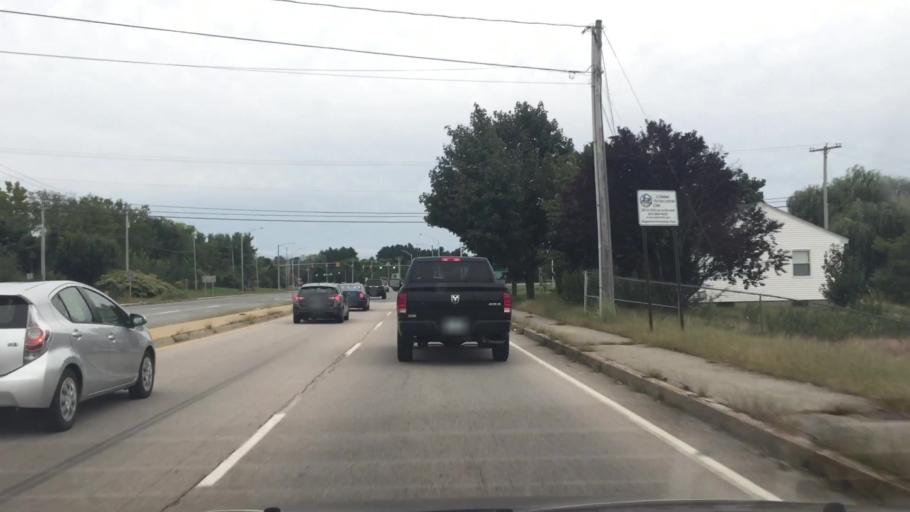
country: US
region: New Hampshire
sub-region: Hillsborough County
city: Hudson
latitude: 42.7312
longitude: -71.4253
